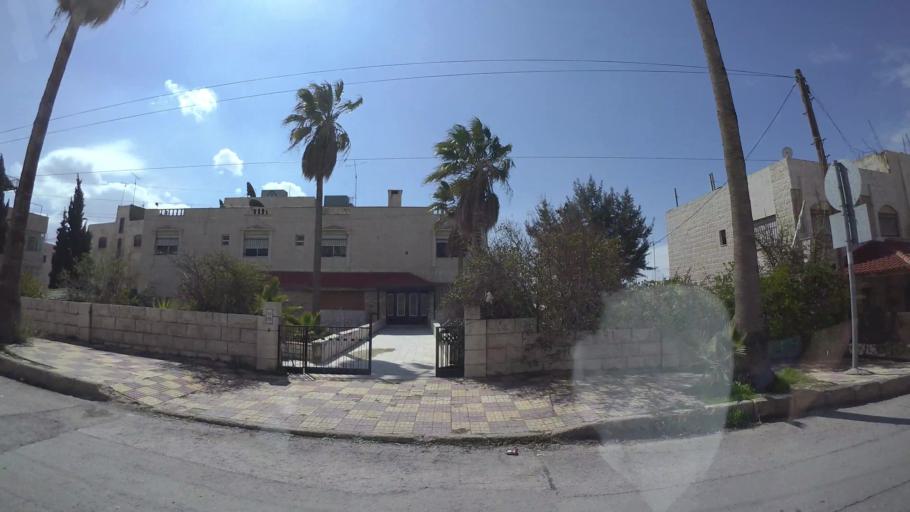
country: JO
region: Amman
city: Amman
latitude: 31.9900
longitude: 35.9053
